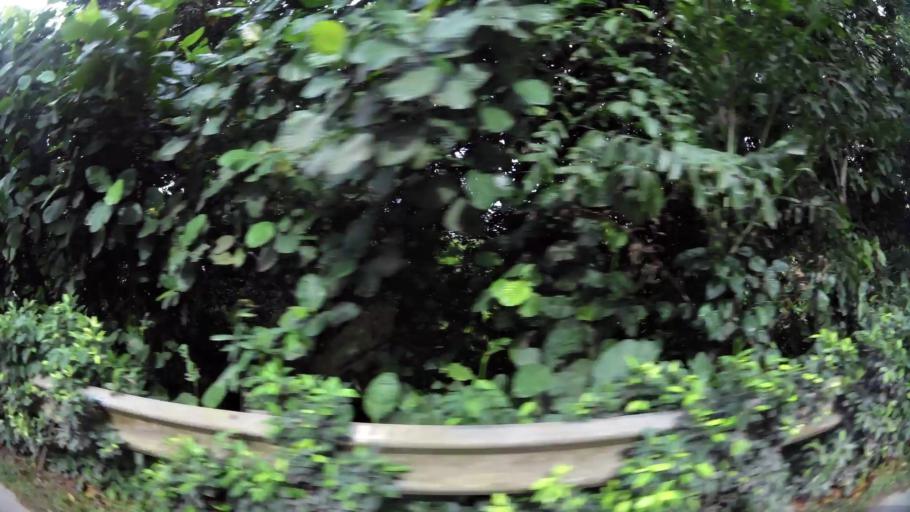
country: MY
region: Johor
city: Johor Bahru
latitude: 1.4097
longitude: 103.7010
